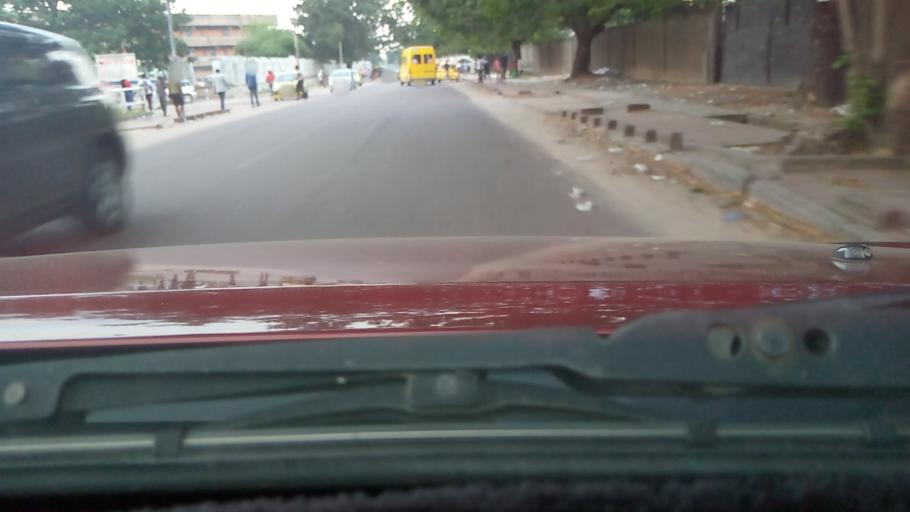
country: CD
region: Kinshasa
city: Kinshasa
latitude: -4.3081
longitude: 15.2848
